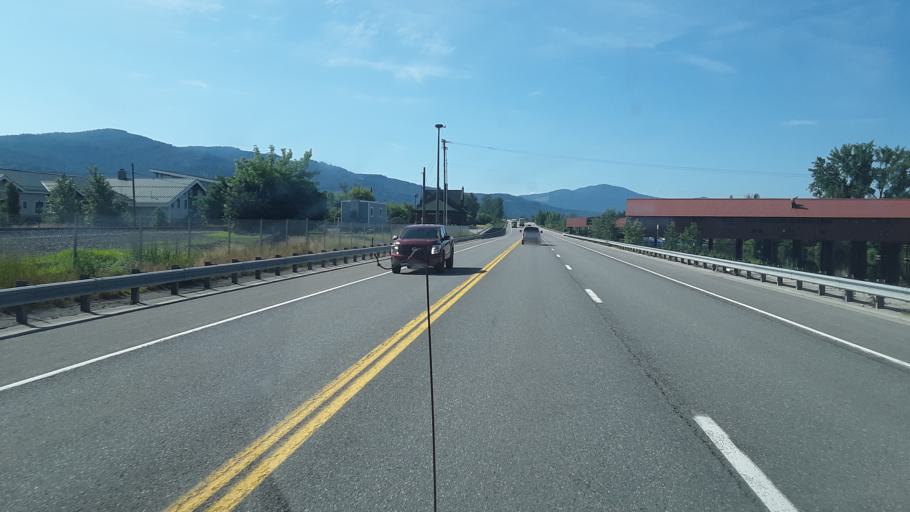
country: US
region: Idaho
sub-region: Bonner County
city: Sandpoint
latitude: 48.2784
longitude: -116.5465
